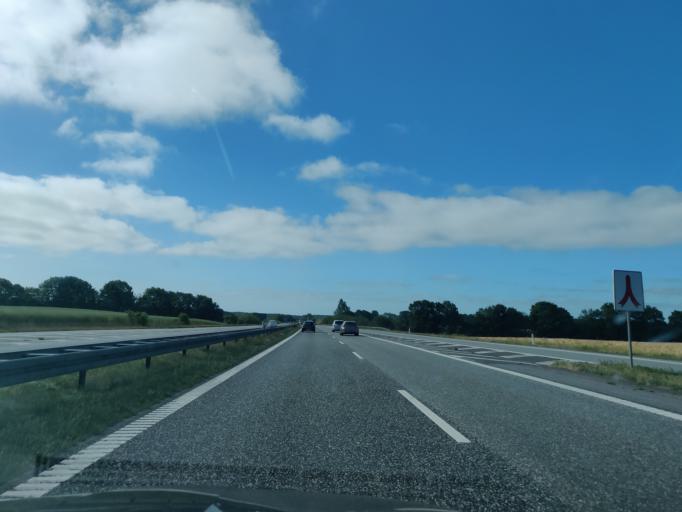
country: DK
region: North Denmark
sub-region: Mariagerfjord Kommune
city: Hobro
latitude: 56.6650
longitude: 9.7341
